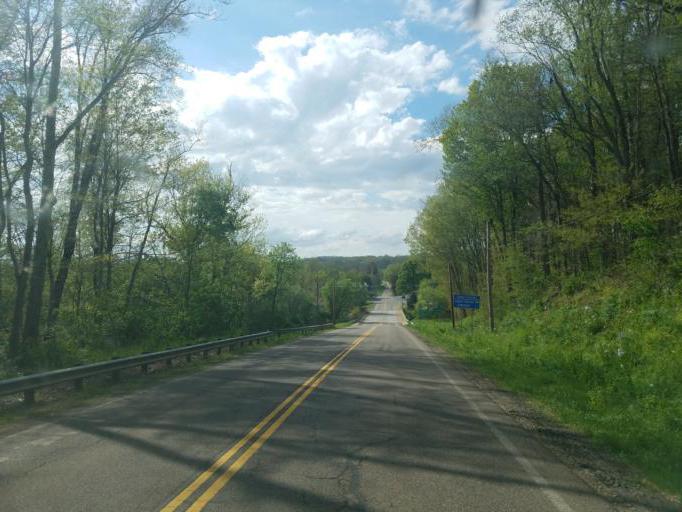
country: US
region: Ohio
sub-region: Knox County
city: Oak Hill
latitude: 40.3982
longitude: -82.2751
